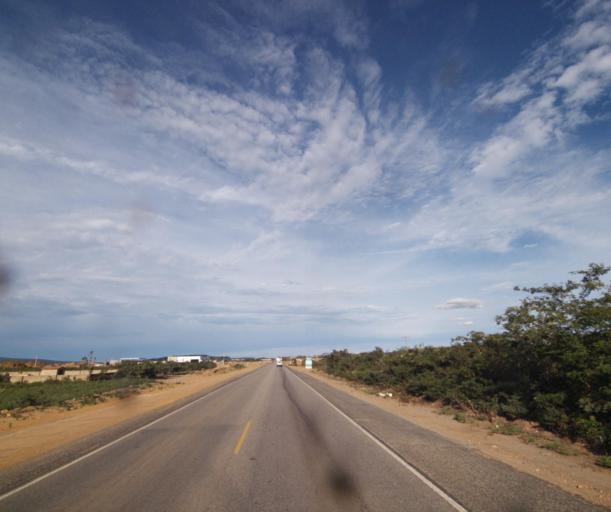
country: BR
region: Bahia
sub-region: Caetite
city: Caetite
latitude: -14.0743
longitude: -42.5440
